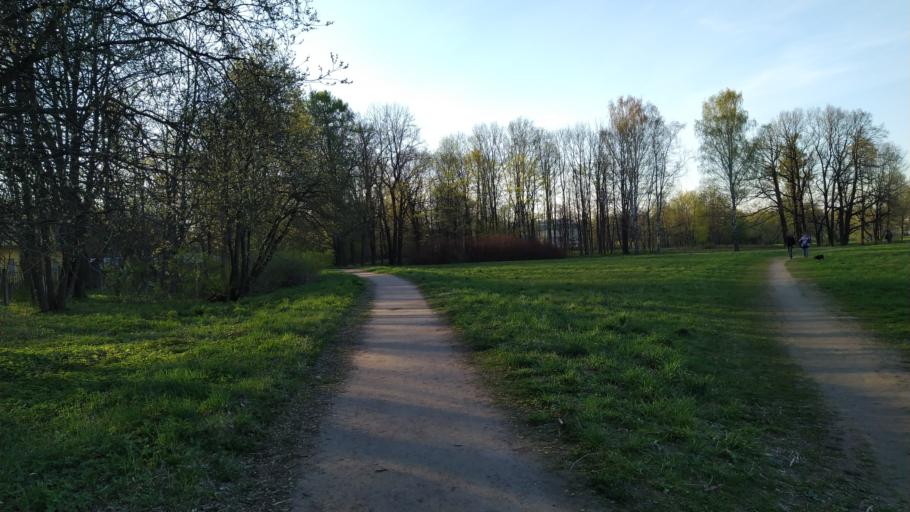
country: RU
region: St.-Petersburg
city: Pushkin
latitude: 59.7088
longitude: 30.4194
